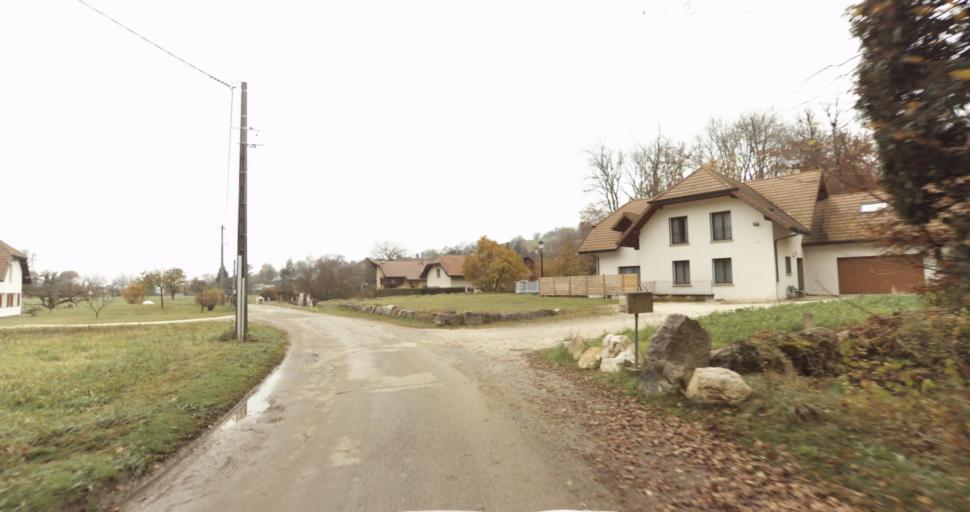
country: FR
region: Rhone-Alpes
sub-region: Departement de la Haute-Savoie
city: Cusy
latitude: 45.7543
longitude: 6.0057
